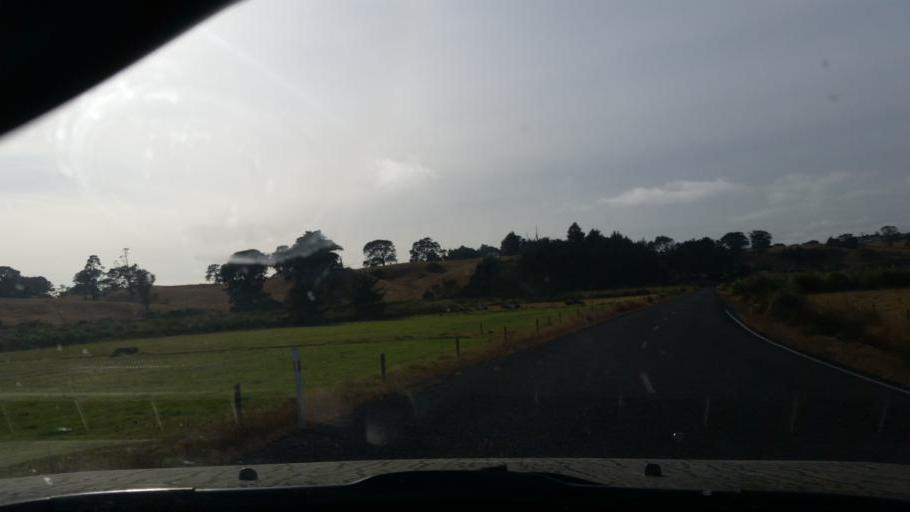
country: NZ
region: Northland
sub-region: Kaipara District
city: Dargaville
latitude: -36.1917
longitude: 174.0407
